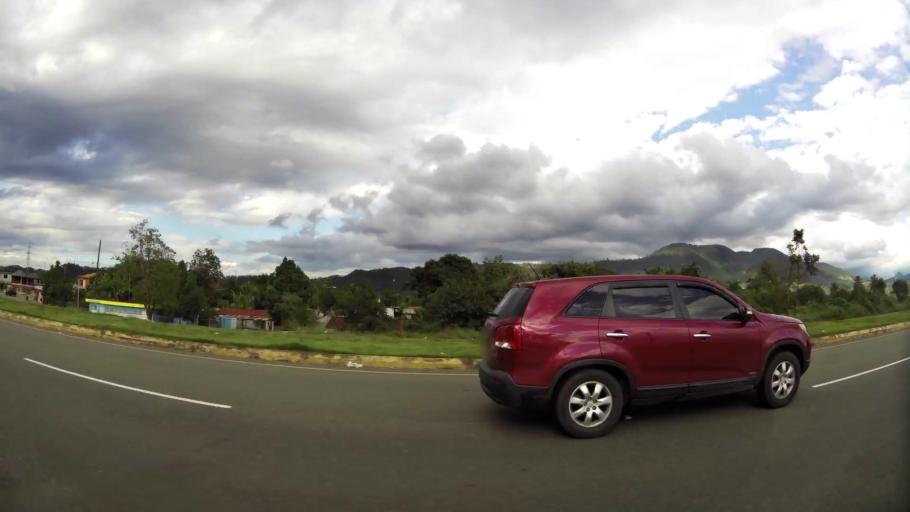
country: DO
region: Monsenor Nouel
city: Bonao
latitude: 18.9038
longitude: -70.3728
